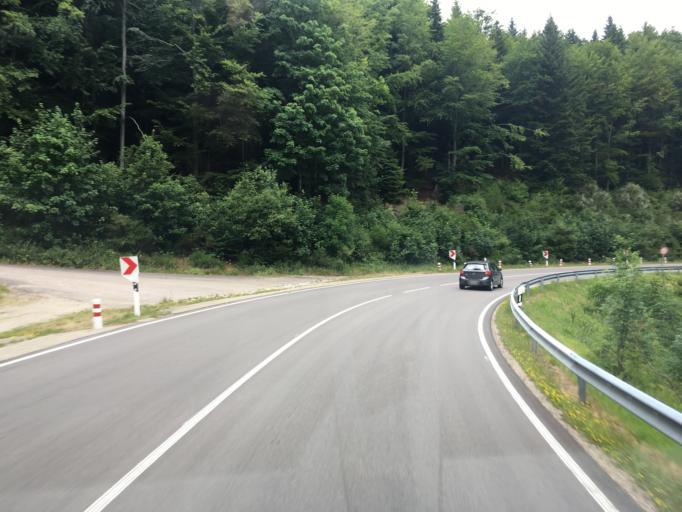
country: DE
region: Baden-Wuerttemberg
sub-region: Karlsruhe Region
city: Buhlertal
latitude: 48.6939
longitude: 8.2313
